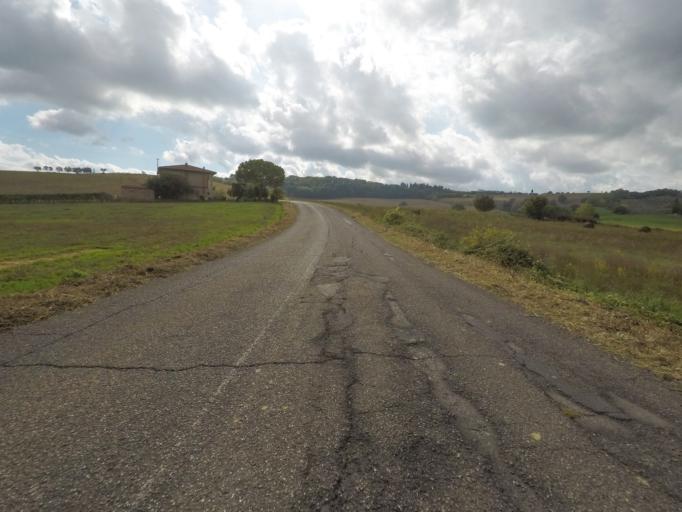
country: IT
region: Tuscany
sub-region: Provincia di Siena
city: Torrita di Siena
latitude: 43.1597
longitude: 11.7736
